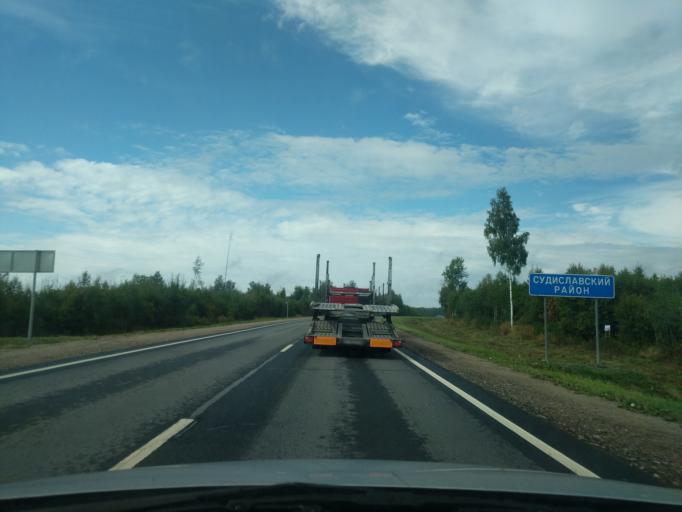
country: RU
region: Kostroma
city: Sudislavl'
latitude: 57.8227
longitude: 41.9010
